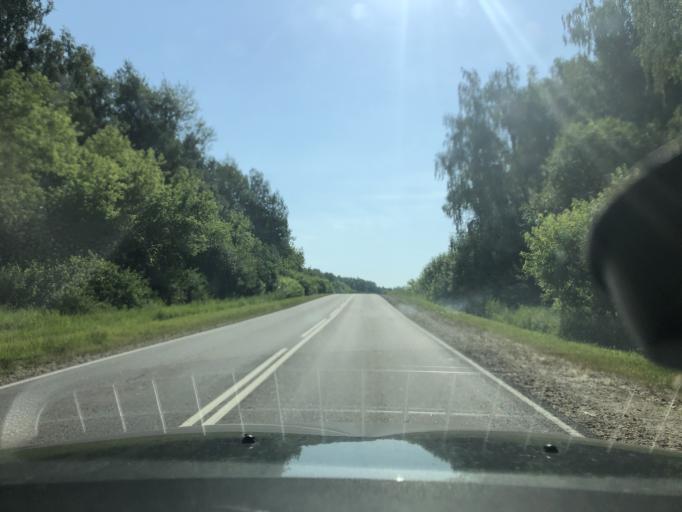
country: RU
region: Tula
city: Dubna
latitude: 54.1291
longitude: 37.0518
